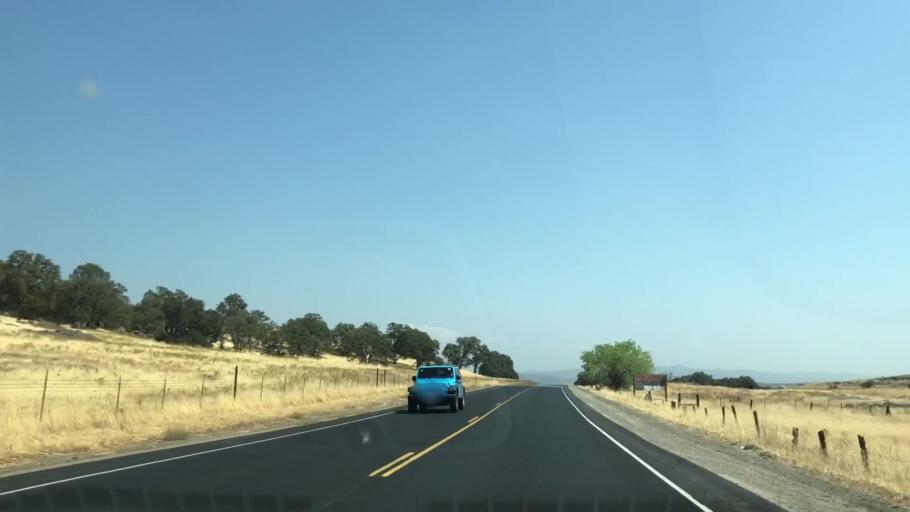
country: US
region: California
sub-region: Tuolumne County
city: Jamestown
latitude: 37.8803
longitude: -120.4684
